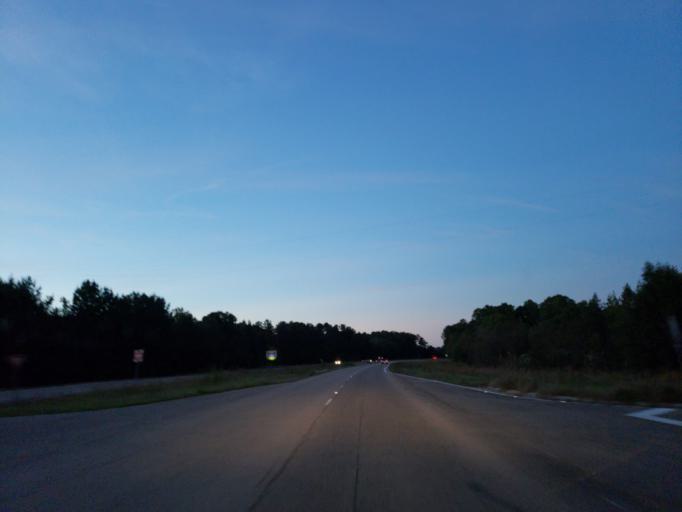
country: US
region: Mississippi
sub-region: Clarke County
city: Quitman
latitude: 31.8548
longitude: -88.7196
